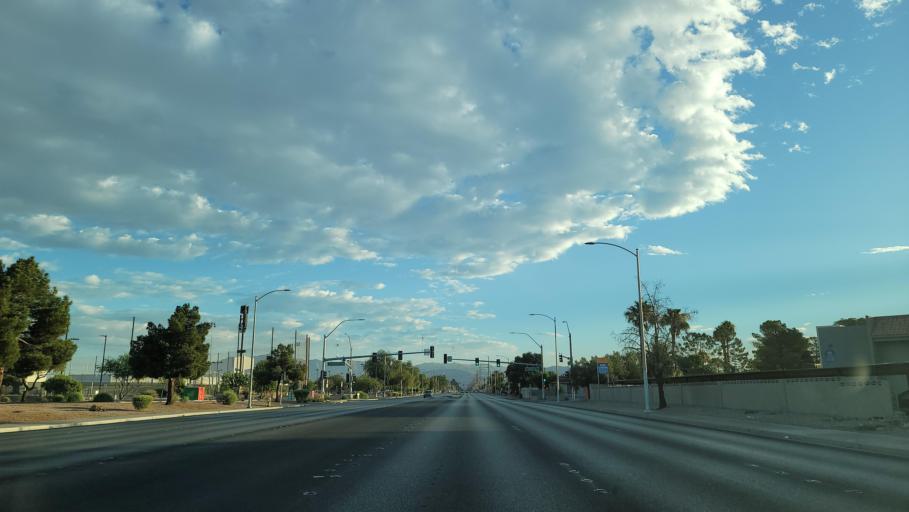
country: US
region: Nevada
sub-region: Clark County
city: North Las Vegas
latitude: 36.1762
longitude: -115.0982
